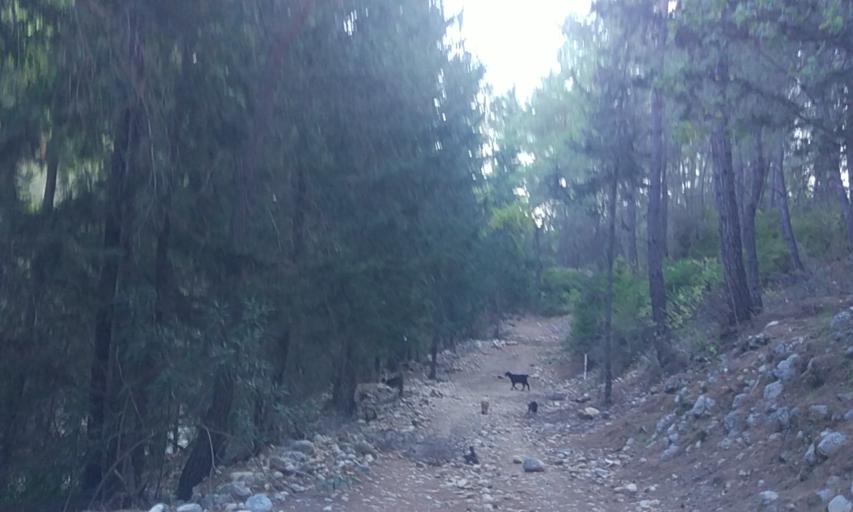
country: TR
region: Antalya
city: Tekirova
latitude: 36.4389
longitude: 30.4414
